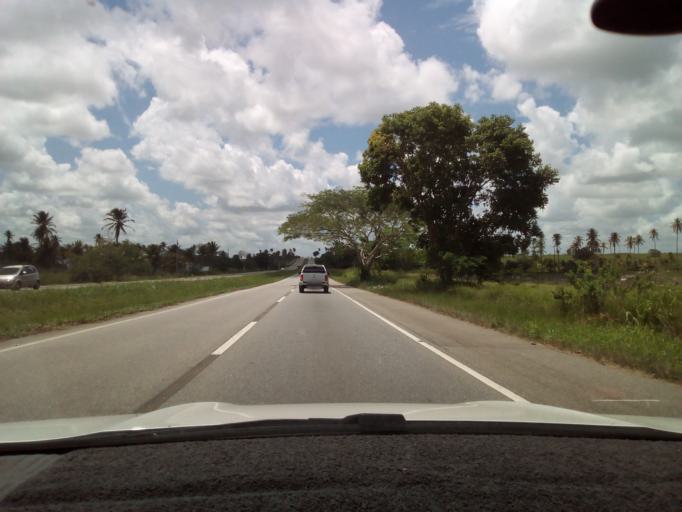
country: BR
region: Paraiba
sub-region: Pilar
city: Pilar
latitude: -7.1903
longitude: -35.2494
